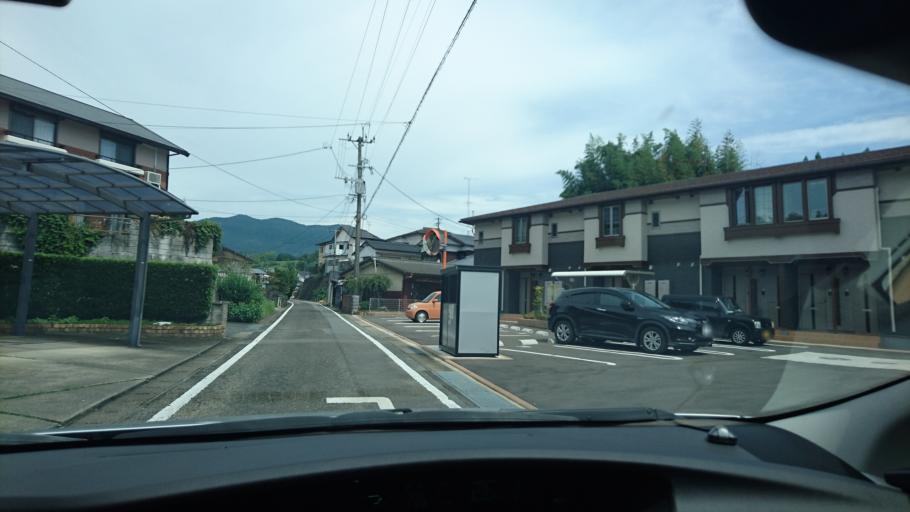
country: JP
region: Saga Prefecture
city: Takeocho-takeo
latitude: 33.2226
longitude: 130.0694
